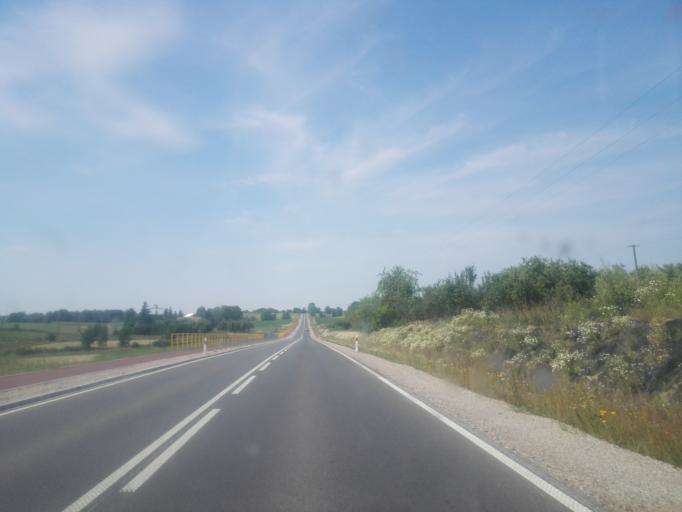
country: PL
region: Podlasie
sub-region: Powiat sejnenski
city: Sejny
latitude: 54.1094
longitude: 23.3026
